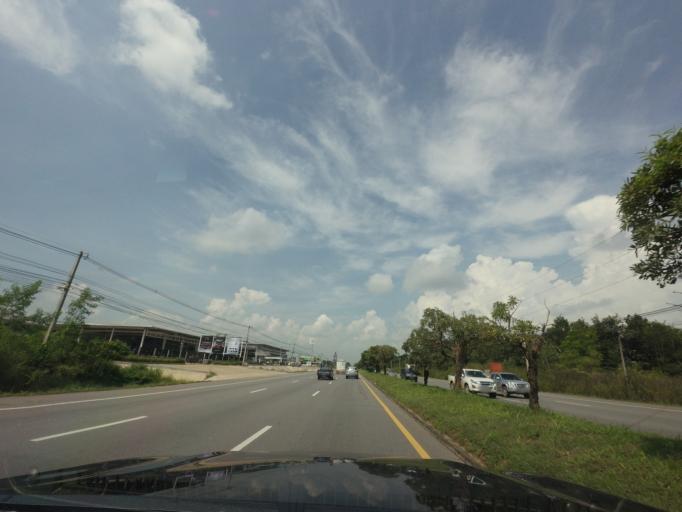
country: TH
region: Khon Kaen
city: Khon Kaen
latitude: 16.4507
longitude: 102.7431
